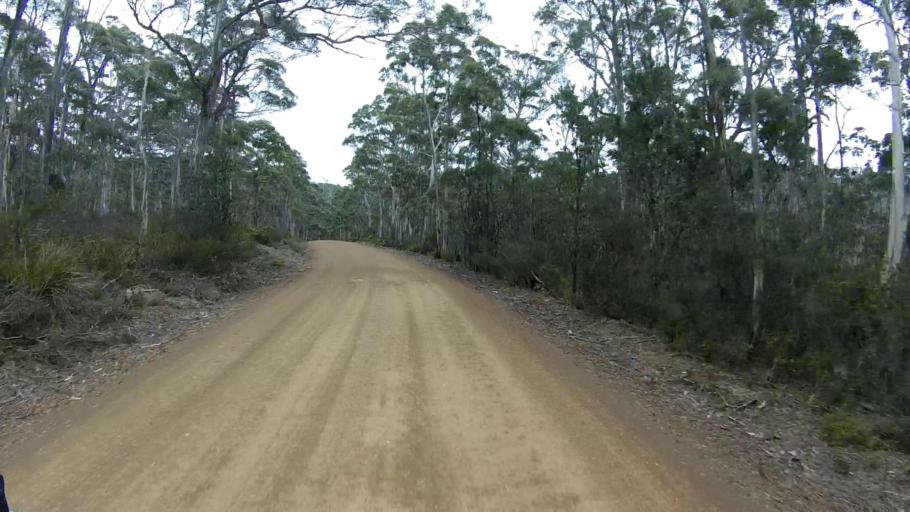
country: AU
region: Tasmania
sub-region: Sorell
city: Sorell
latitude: -42.6084
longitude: 147.8801
